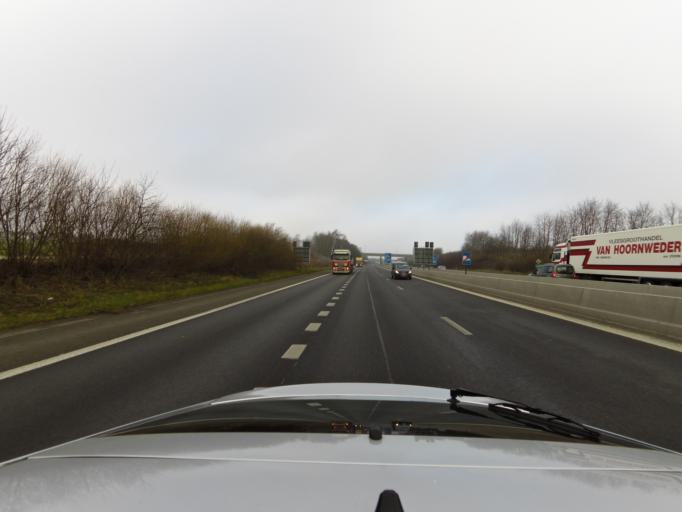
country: BE
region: Flanders
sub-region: Provincie West-Vlaanderen
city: Wevelgem
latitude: 50.7974
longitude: 3.2181
